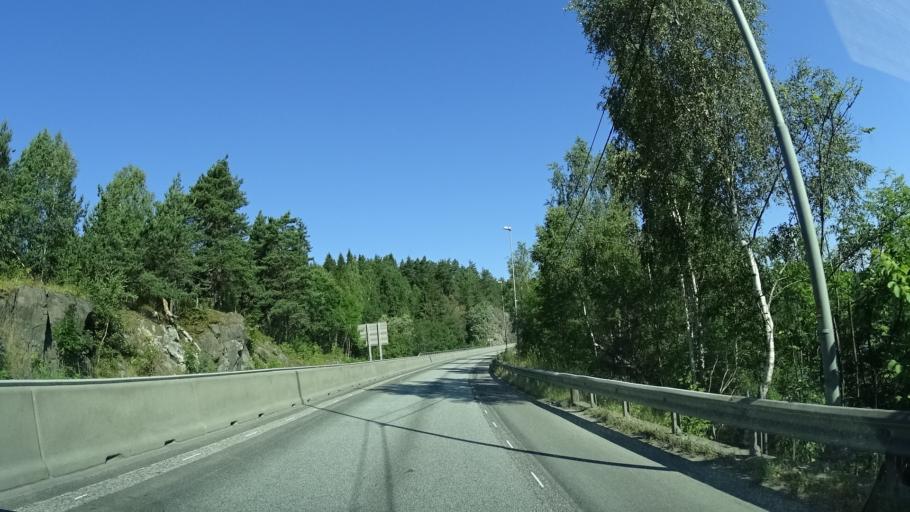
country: NO
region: Akershus
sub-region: Oppegard
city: Kolbotn
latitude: 59.7586
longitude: 10.7767
